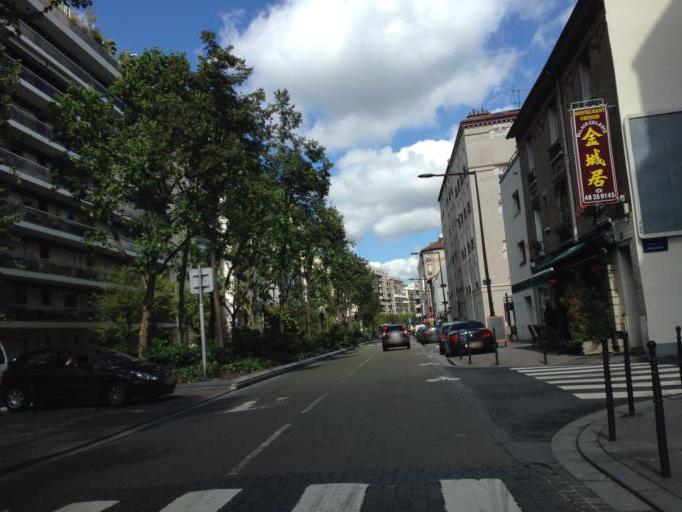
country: FR
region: Ile-de-France
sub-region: Departement des Hauts-de-Seine
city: Boulogne-Billancourt
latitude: 48.8336
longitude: 2.2333
